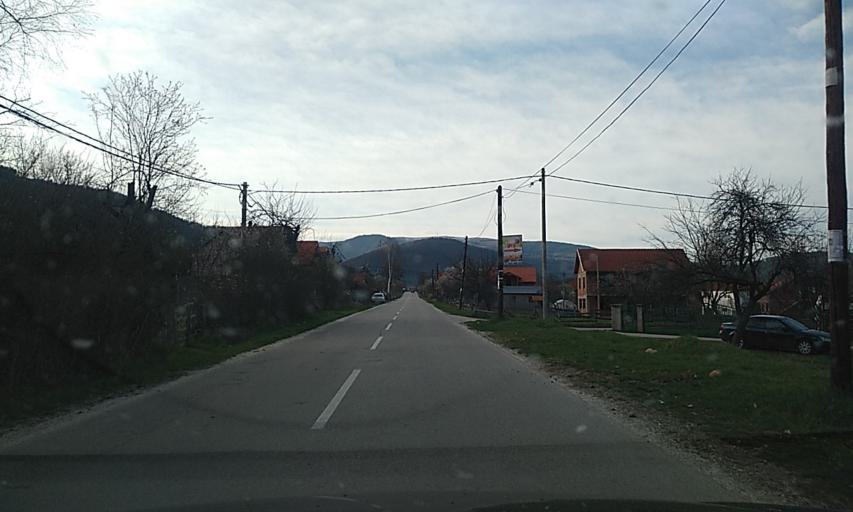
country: RS
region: Central Serbia
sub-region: Pcinjski Okrug
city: Bosilegrad
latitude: 42.4772
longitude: 22.4788
